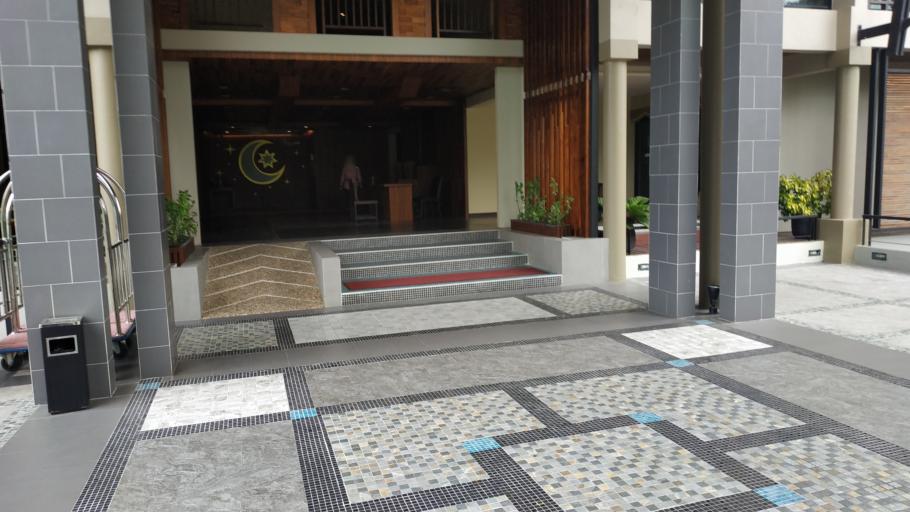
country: TH
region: Phangnga
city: Ban Ao Nang
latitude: 8.0373
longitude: 98.8307
